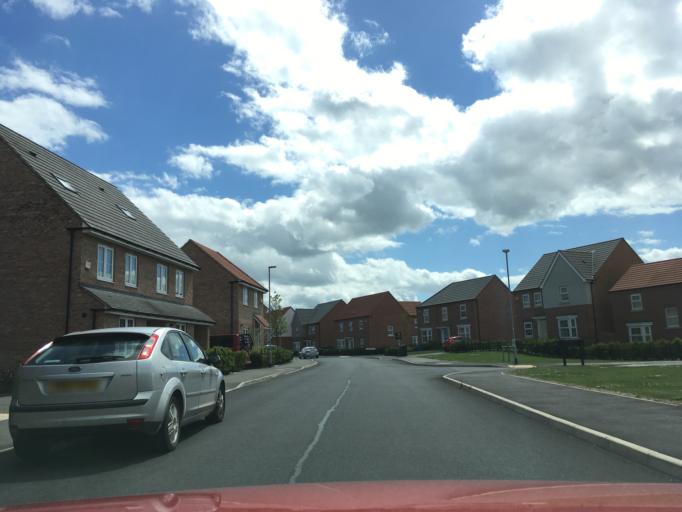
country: GB
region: England
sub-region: Nottinghamshire
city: Cotgrave
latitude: 52.9189
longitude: -1.0316
